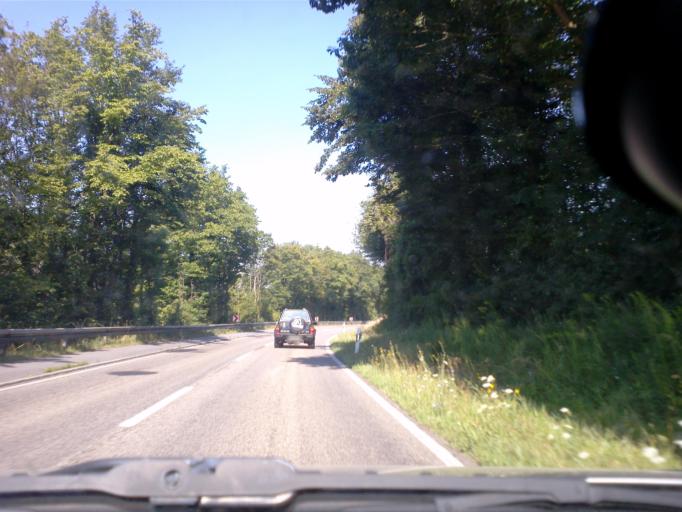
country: DE
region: Baden-Wuerttemberg
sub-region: Karlsruhe Region
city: Weingarten
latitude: 49.0824
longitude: 8.5636
